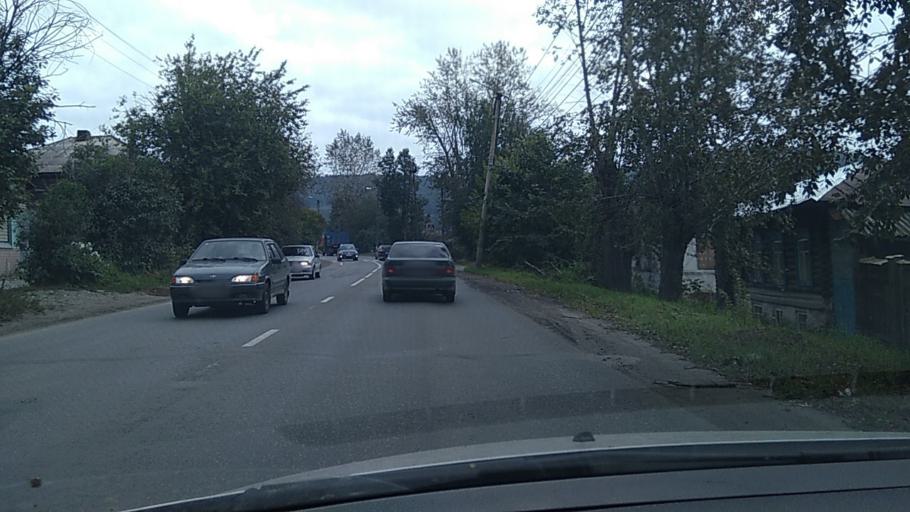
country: RU
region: Chelyabinsk
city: Zlatoust
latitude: 55.1766
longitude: 59.6951
